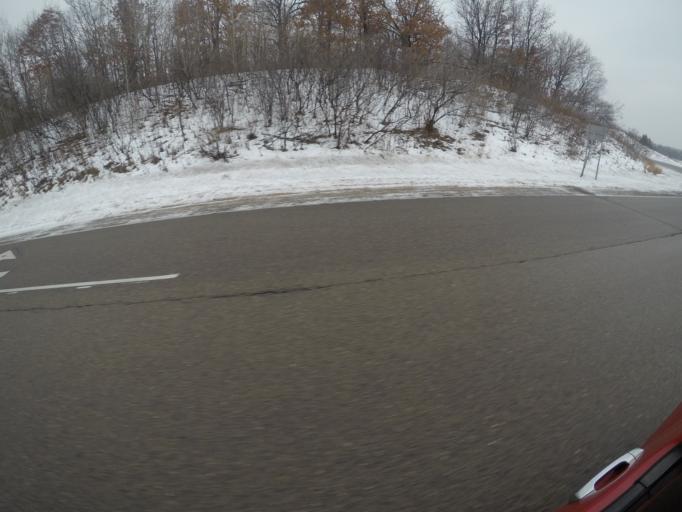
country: US
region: Minnesota
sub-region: Dakota County
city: Mendota Heights
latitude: 44.8609
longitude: -93.1274
